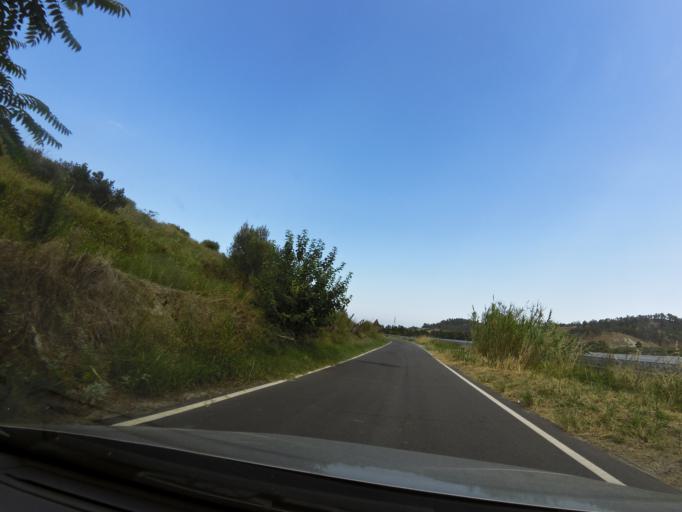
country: IT
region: Calabria
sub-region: Provincia di Reggio Calabria
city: Camini
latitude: 38.4293
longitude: 16.5190
